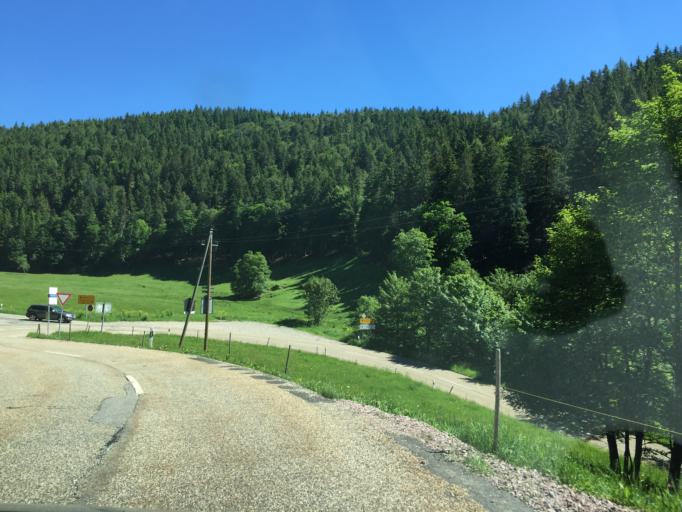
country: DE
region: Baden-Wuerttemberg
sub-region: Freiburg Region
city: Bollen
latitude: 47.8225
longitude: 7.8543
